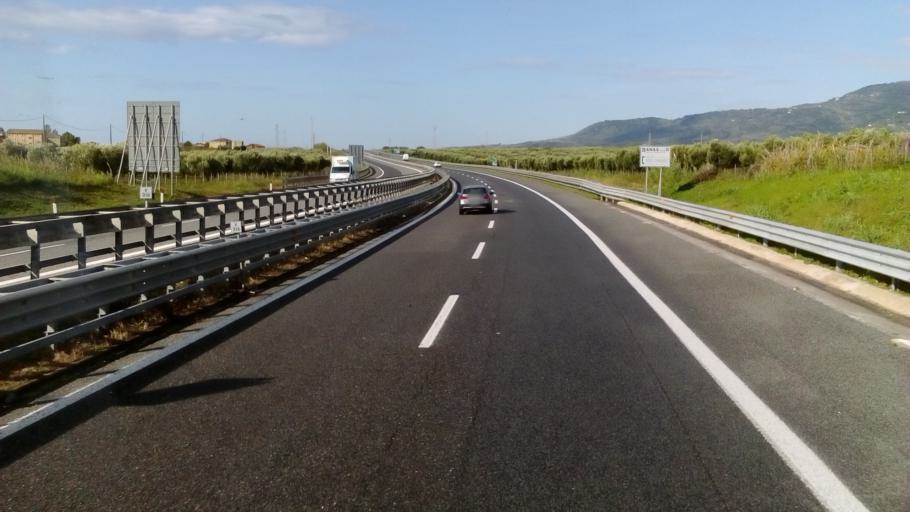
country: IT
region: Calabria
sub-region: Provincia di Catanzaro
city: Santa Eufemia Lamezia
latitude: 38.9231
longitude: 16.2600
